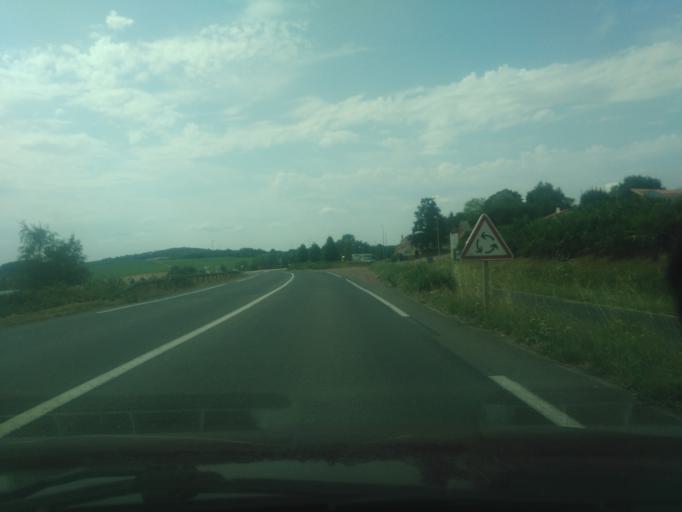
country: FR
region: Pays de la Loire
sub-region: Departement de la Vendee
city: Antigny
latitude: 46.6606
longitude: -0.7869
